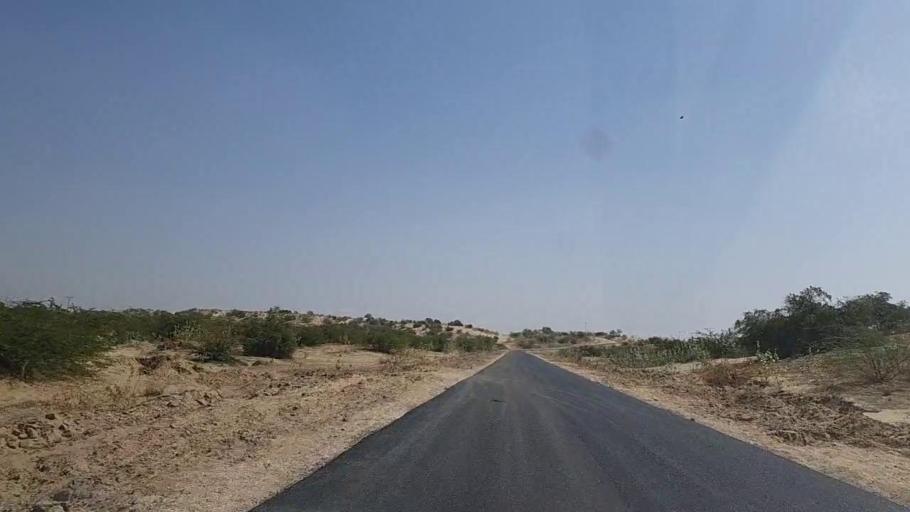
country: PK
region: Sindh
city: Diplo
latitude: 24.4811
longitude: 69.5247
